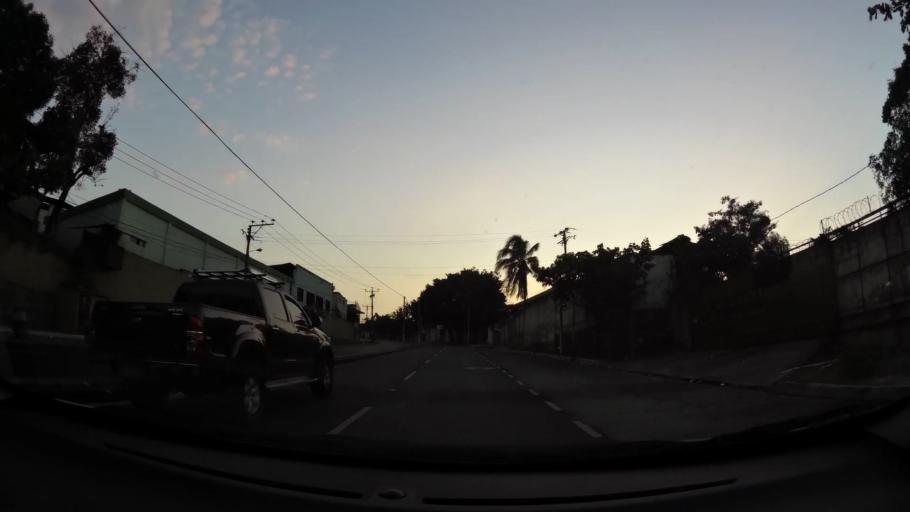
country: SV
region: San Salvador
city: Delgado
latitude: 13.7067
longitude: -89.1785
